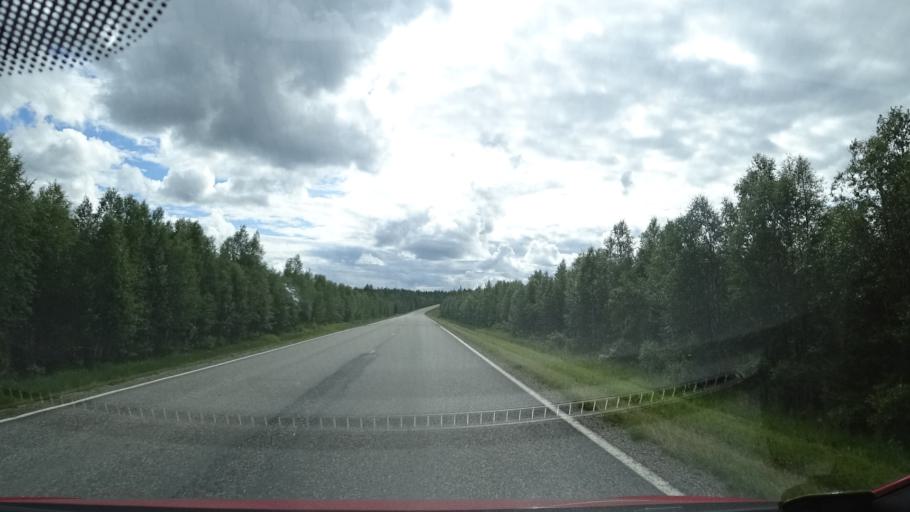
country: FI
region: Lapland
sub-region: Tunturi-Lappi
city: Kittilae
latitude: 67.5632
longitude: 24.9206
